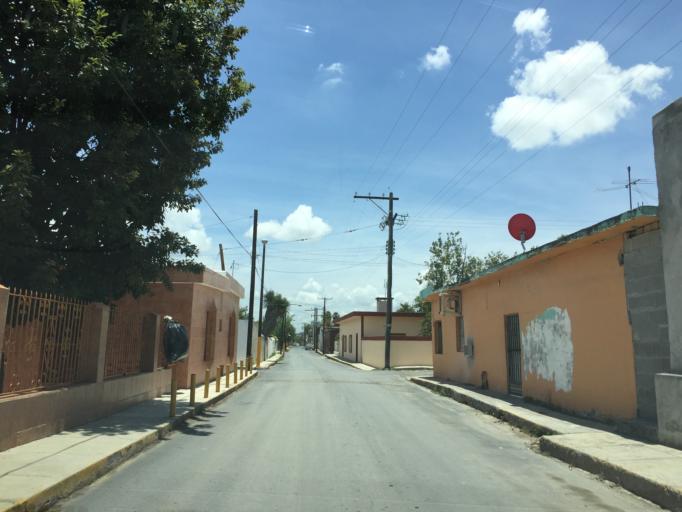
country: MX
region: Nuevo Leon
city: Marin
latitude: 25.8602
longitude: -99.9446
